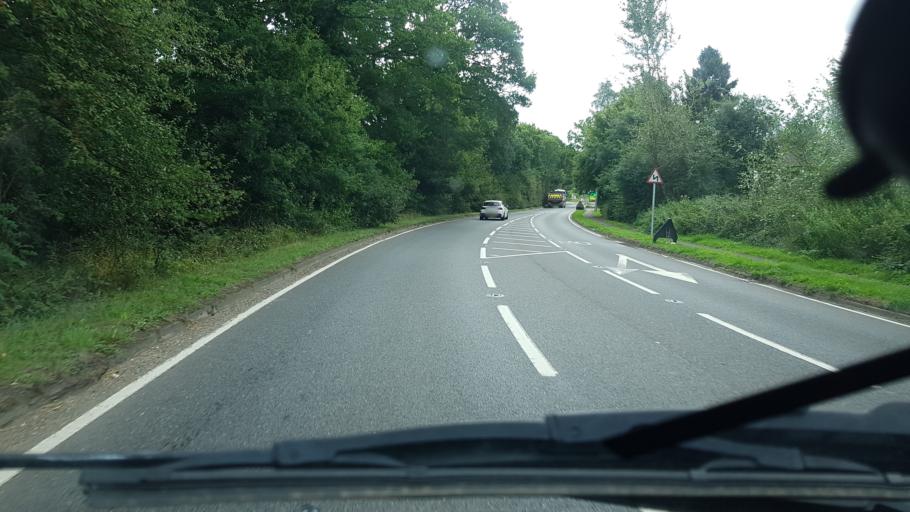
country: GB
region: England
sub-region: Surrey
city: Cranleigh
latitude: 51.1064
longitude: -0.5109
